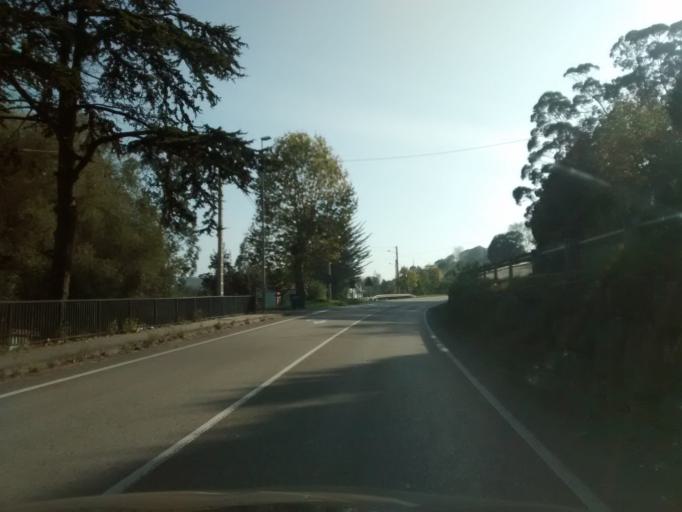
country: ES
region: Cantabria
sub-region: Provincia de Cantabria
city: Miengo
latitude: 43.4232
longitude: -3.9619
